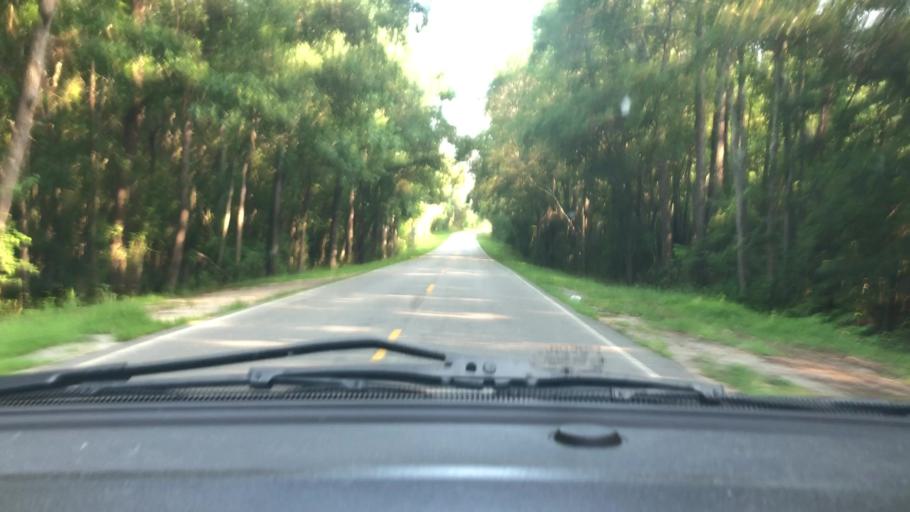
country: US
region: North Carolina
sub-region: Lee County
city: Broadway
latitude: 35.3338
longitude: -79.0725
